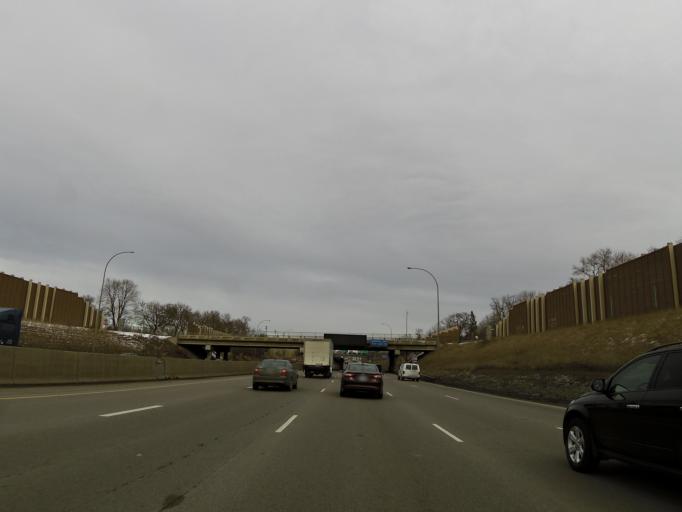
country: US
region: Minnesota
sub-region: Hennepin County
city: Richfield
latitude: 44.9257
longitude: -93.2746
